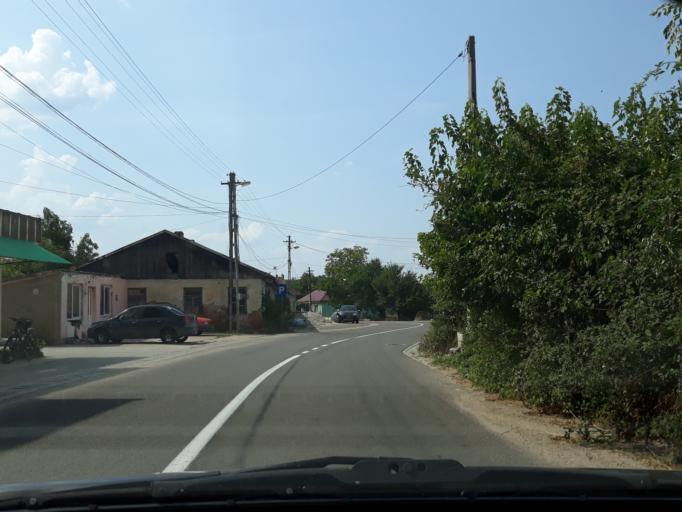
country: RO
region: Bihor
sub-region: Comuna Pietroasa
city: Pietroasa
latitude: 46.5906
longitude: 22.5592
